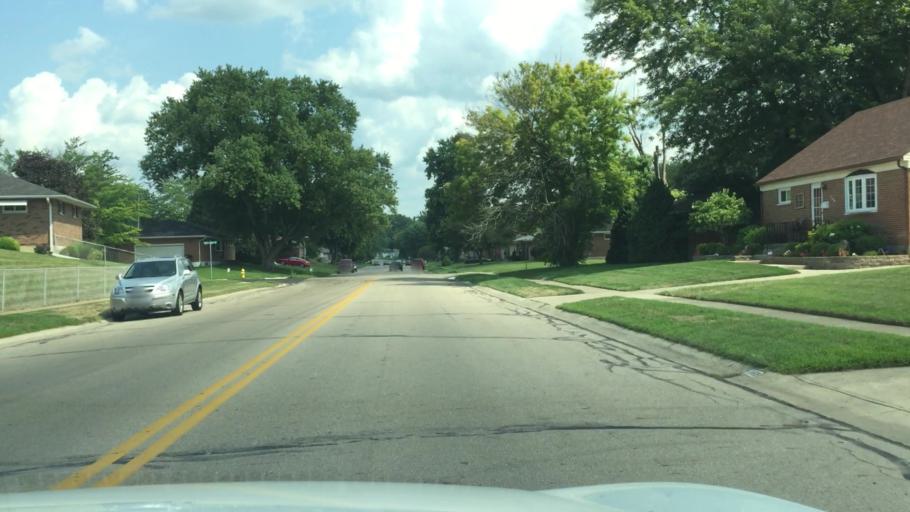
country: US
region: Ohio
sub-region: Clark County
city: Northridge
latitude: 39.9841
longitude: -83.7801
